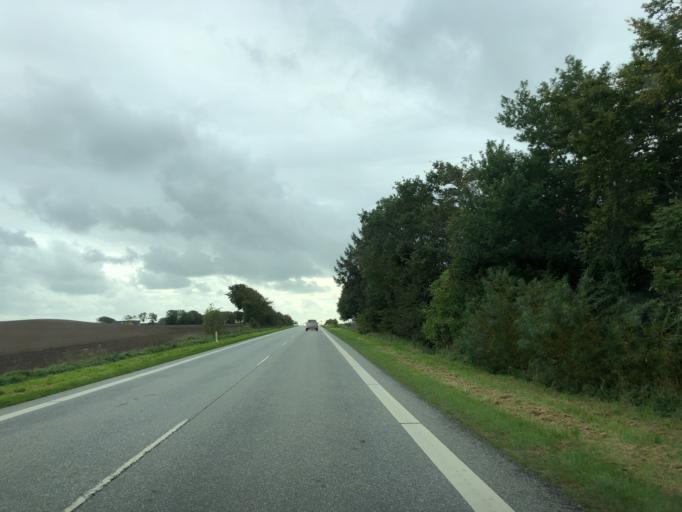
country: DK
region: North Denmark
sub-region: Thisted Kommune
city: Hurup
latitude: 56.8197
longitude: 8.4923
